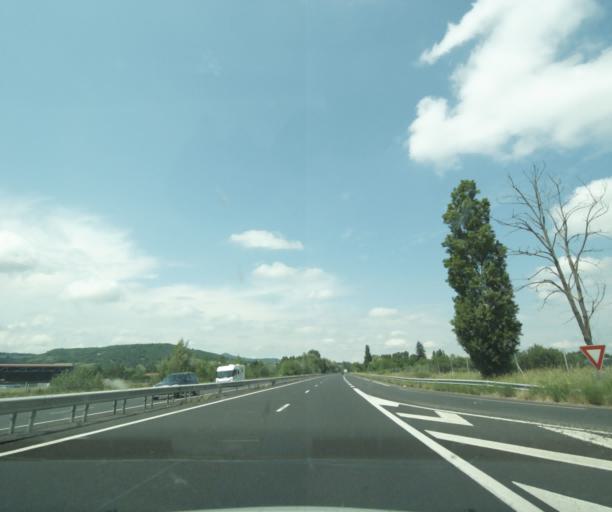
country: FR
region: Auvergne
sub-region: Departement de la Haute-Loire
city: Lempdes-sur-Allagnon
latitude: 45.3865
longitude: 3.2768
